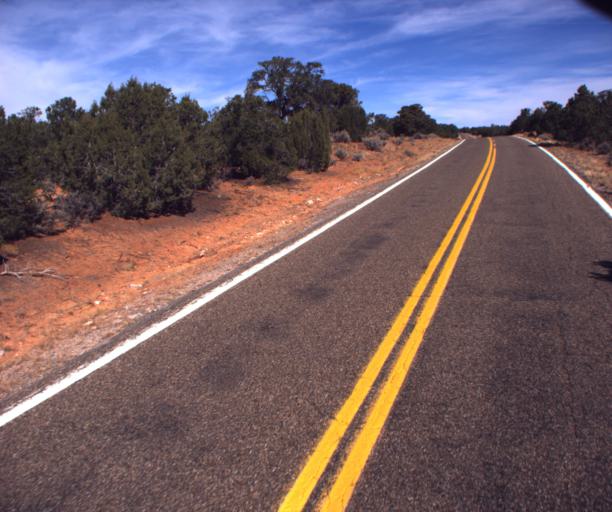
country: US
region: Arizona
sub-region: Navajo County
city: Kayenta
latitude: 36.5782
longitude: -110.4918
